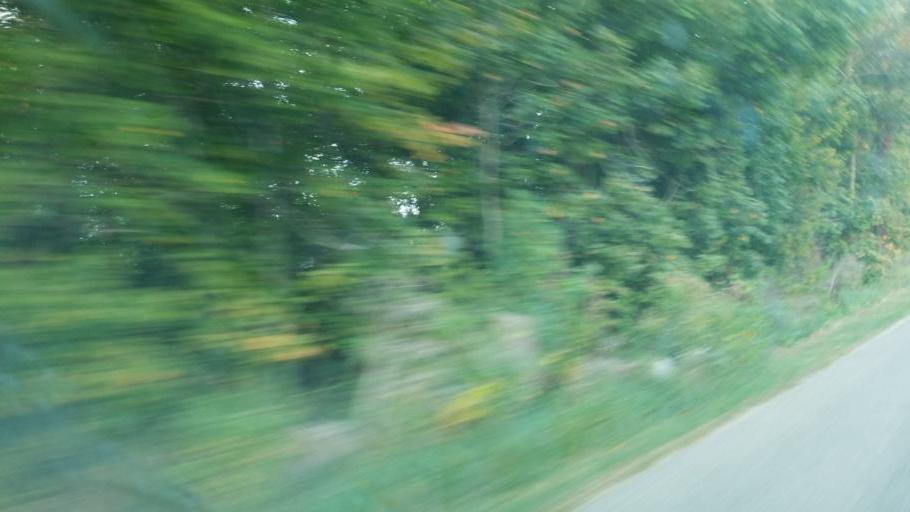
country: US
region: Ohio
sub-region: Knox County
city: Fredericktown
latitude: 40.4606
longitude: -82.6234
